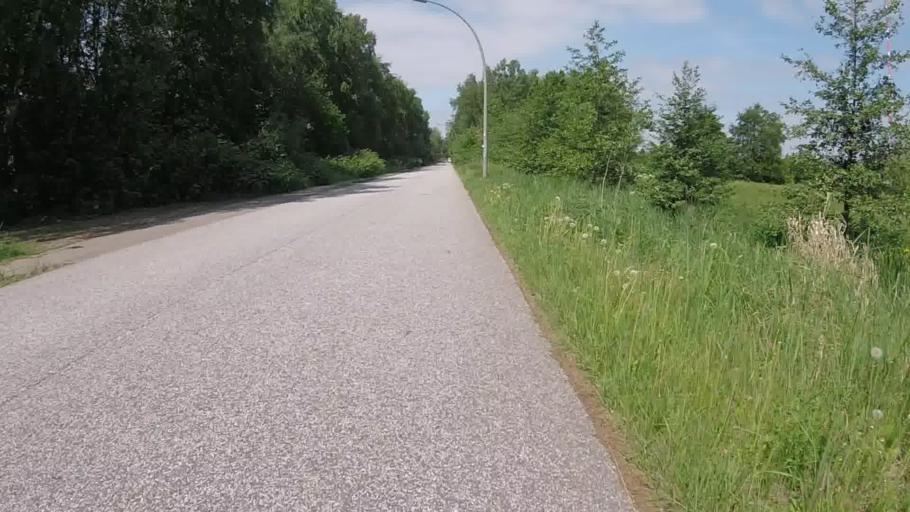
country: DE
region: Hamburg
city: Wandsbek
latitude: 53.5141
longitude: 10.1026
